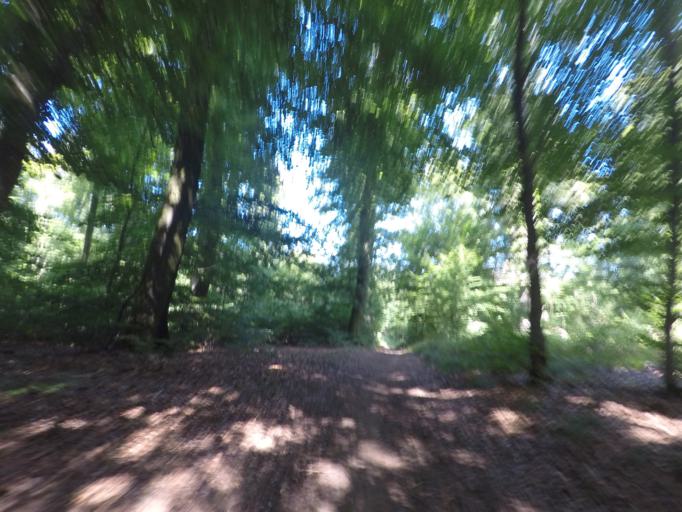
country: LU
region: Luxembourg
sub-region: Canton de Capellen
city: Kopstal
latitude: 49.6461
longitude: 6.0661
